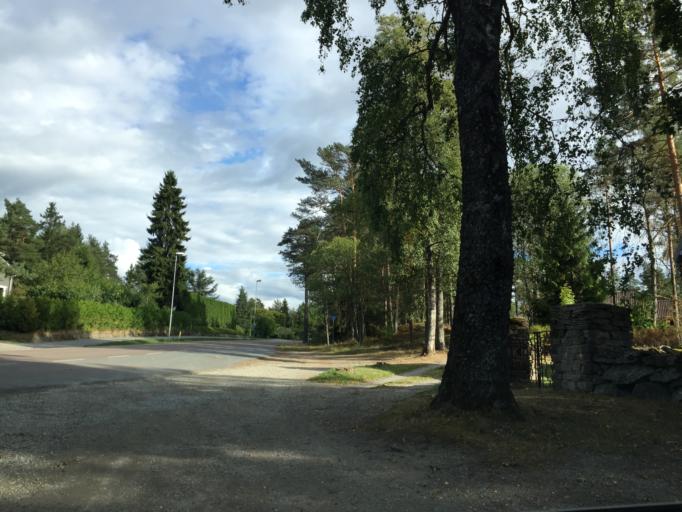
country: NO
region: Ostfold
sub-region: Trogstad
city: Skjonhaug
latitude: 59.6367
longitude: 11.3141
